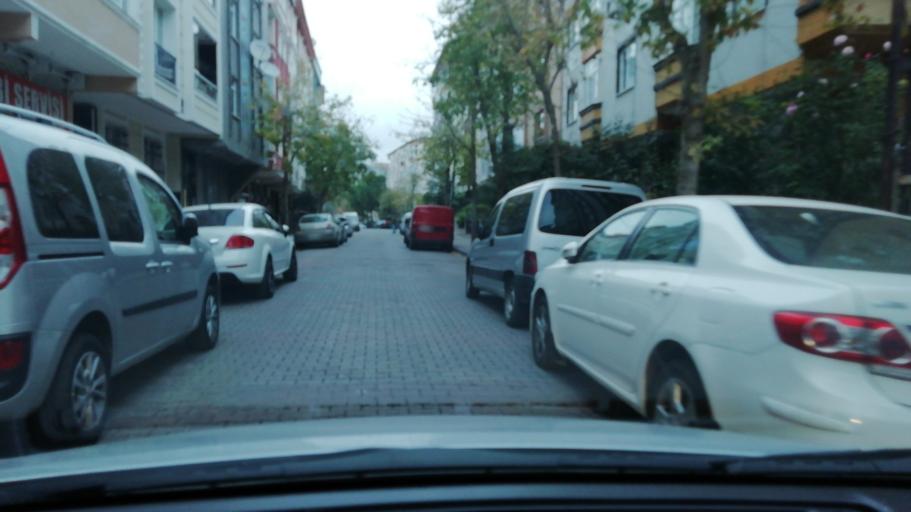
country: TR
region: Istanbul
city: Bagcilar
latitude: 41.0207
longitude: 28.8301
